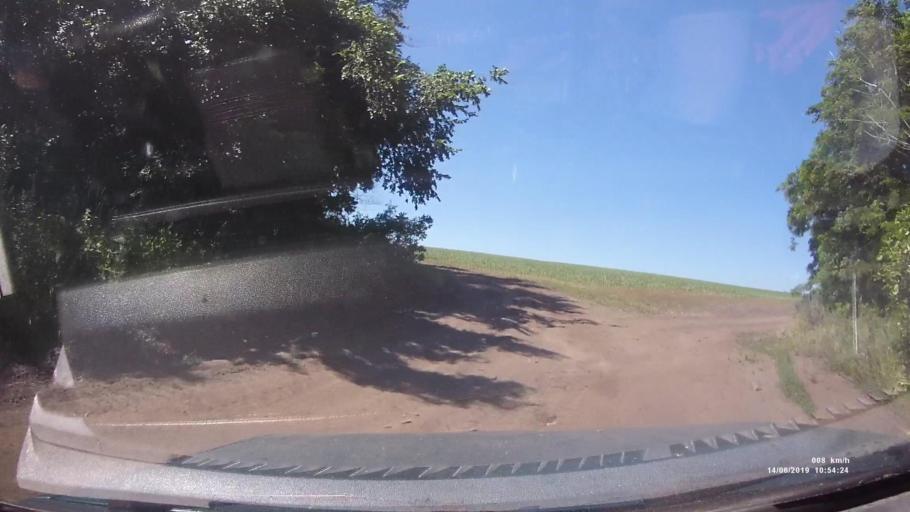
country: RU
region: Rostov
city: Kazanskaya
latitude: 49.8623
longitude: 41.3780
